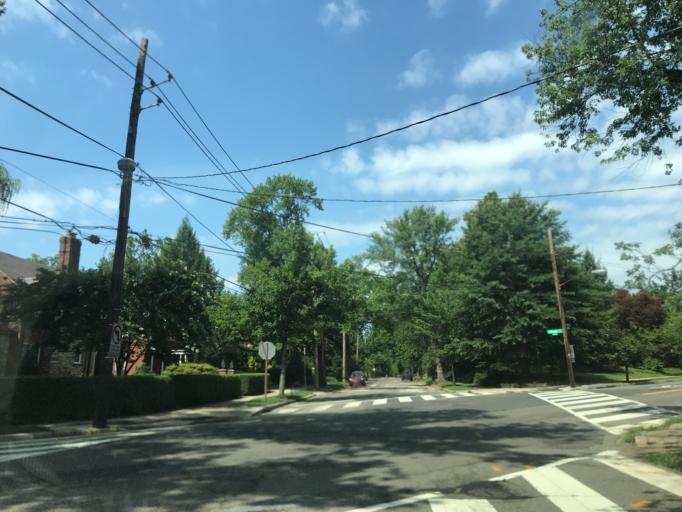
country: US
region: Maryland
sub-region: Montgomery County
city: Friendship Village
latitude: 38.9532
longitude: -77.0865
